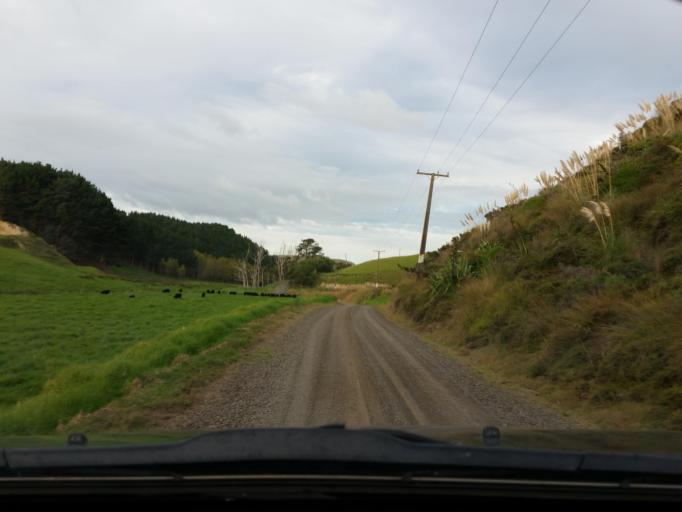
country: NZ
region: Northland
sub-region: Kaipara District
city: Dargaville
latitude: -35.8752
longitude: 173.6806
